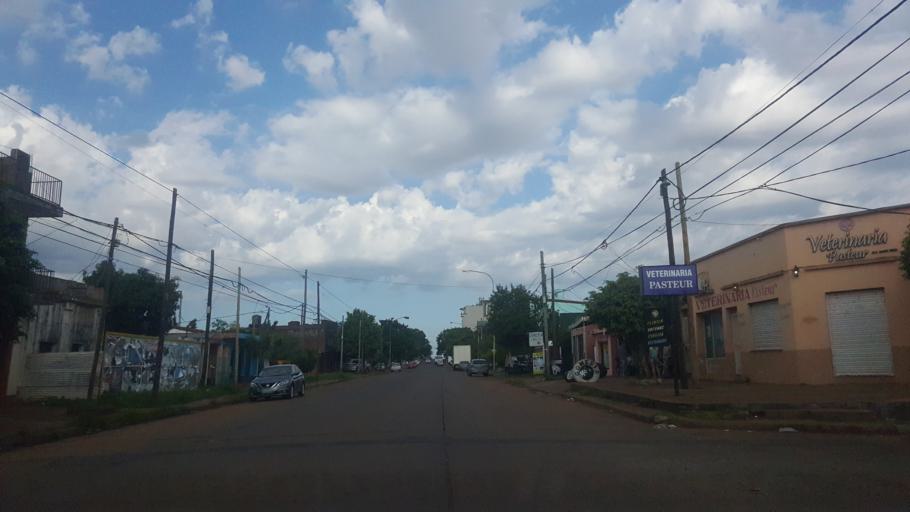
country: AR
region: Misiones
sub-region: Departamento de Capital
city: Posadas
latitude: -27.3878
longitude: -55.8993
